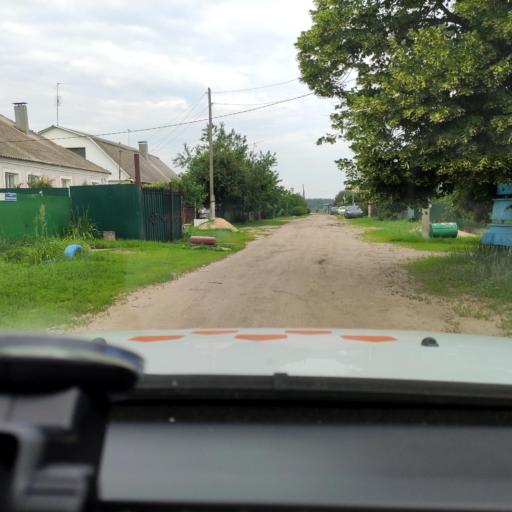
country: RU
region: Voronezj
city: Maslovka
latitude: 51.5806
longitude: 39.3075
